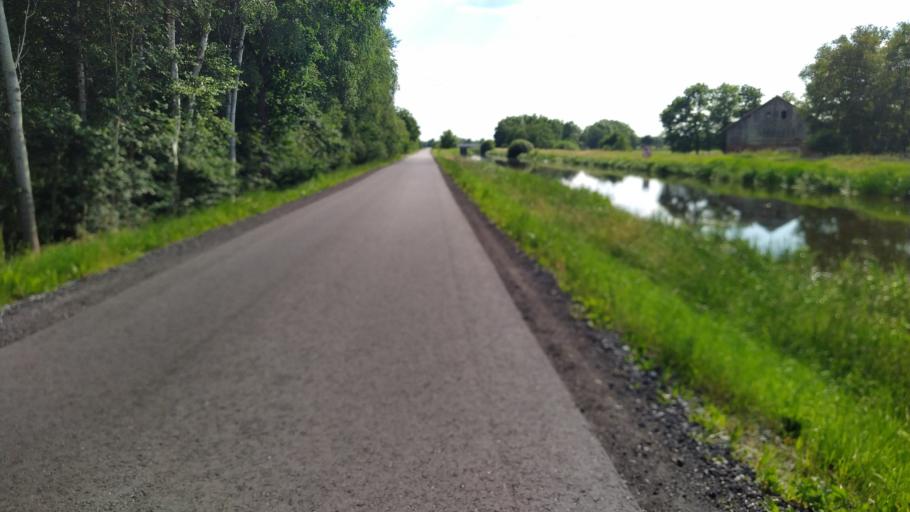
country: DE
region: Lower Saxony
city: Steinau
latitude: 53.6610
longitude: 8.9028
